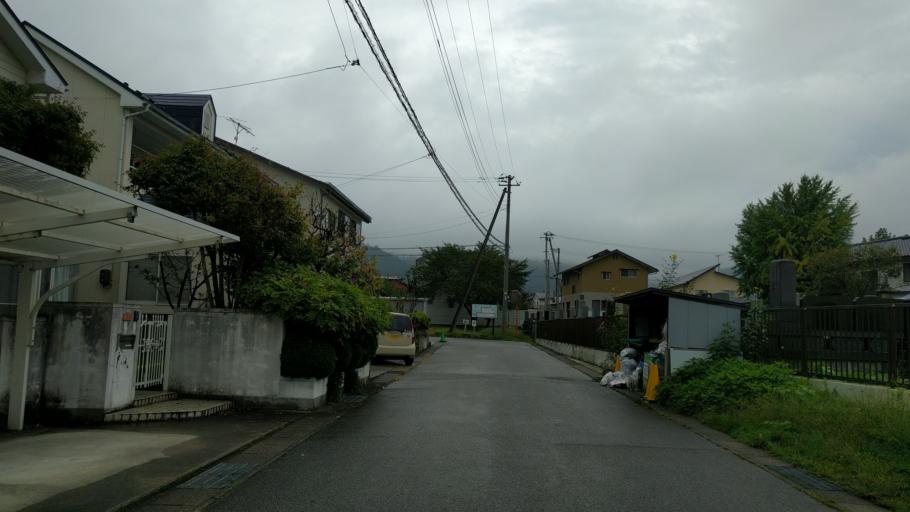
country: JP
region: Fukushima
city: Kitakata
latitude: 37.4902
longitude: 139.9444
